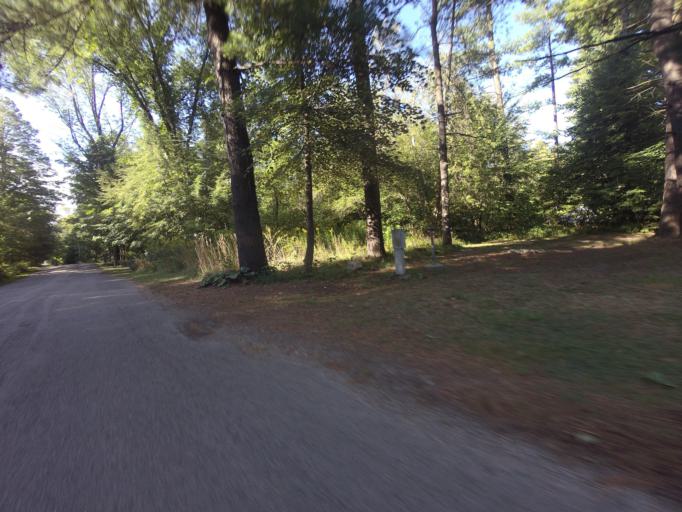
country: CA
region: Ontario
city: Waterloo
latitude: 43.6671
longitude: -80.4499
